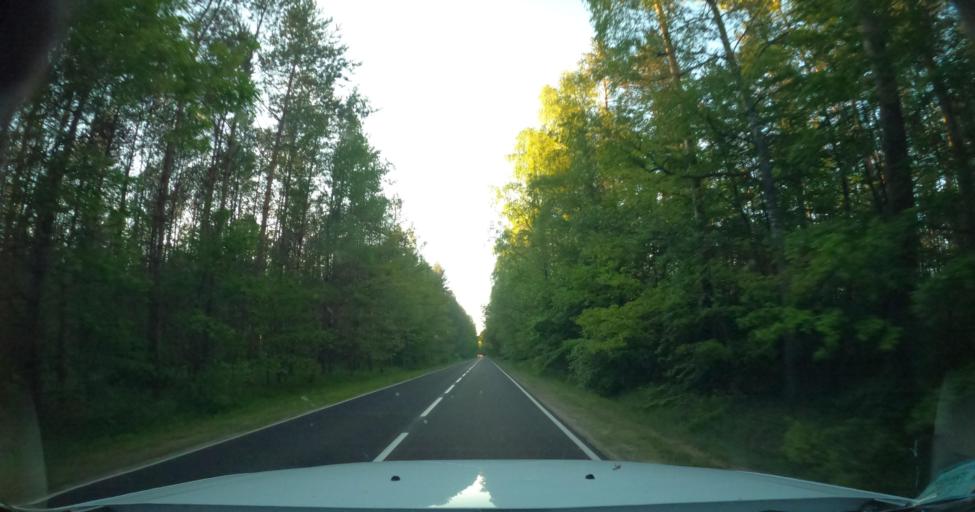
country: PL
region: Pomeranian Voivodeship
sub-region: Powiat slupski
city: Potegowo
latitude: 54.3942
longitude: 17.4709
